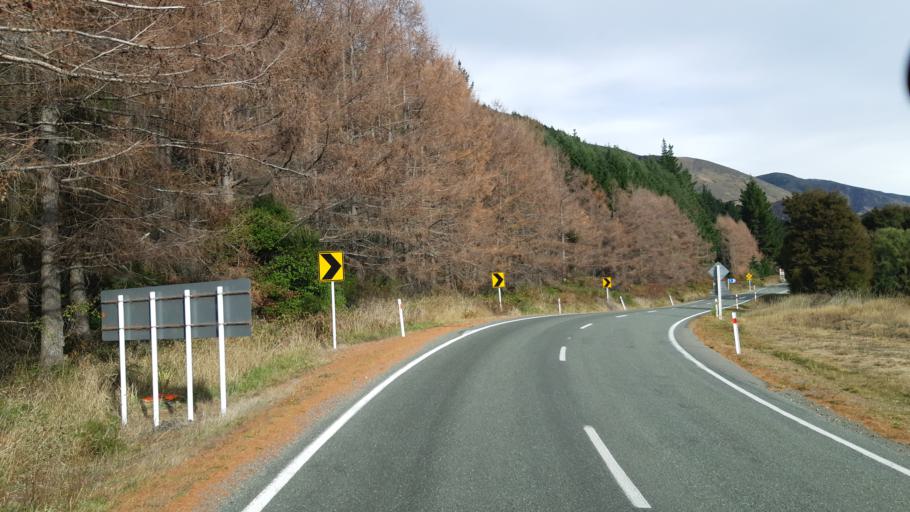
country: NZ
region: Tasman
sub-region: Tasman District
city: Wakefield
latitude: -41.7110
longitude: 173.1144
